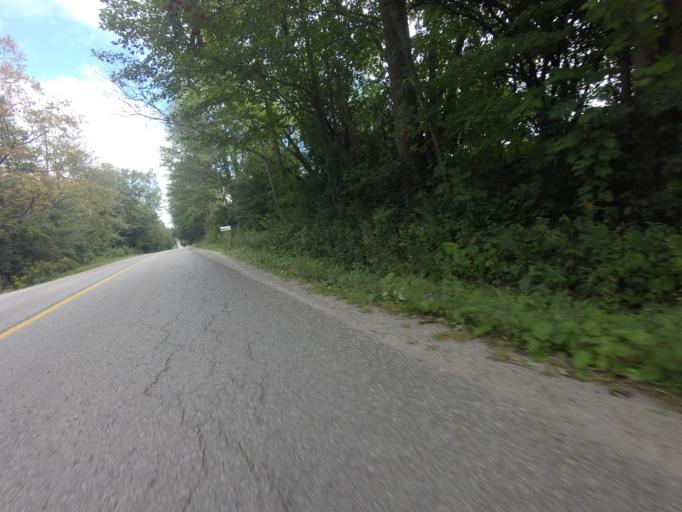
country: CA
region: Ontario
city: Uxbridge
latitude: 44.1232
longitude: -79.1439
